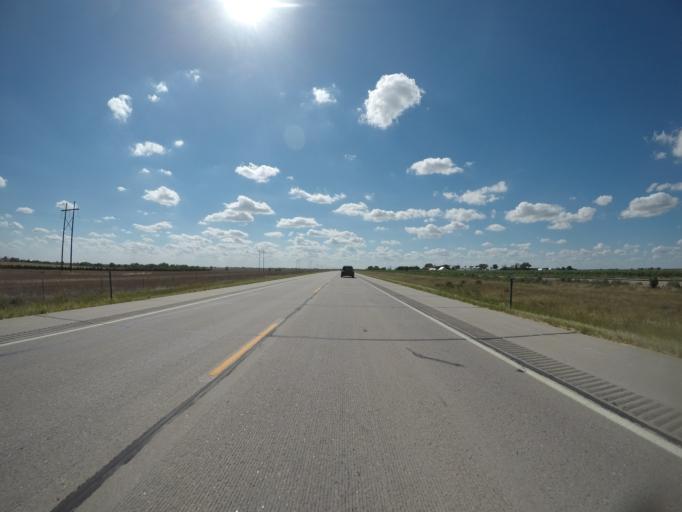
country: US
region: Colorado
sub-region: Phillips County
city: Holyoke
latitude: 40.5923
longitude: -102.3528
